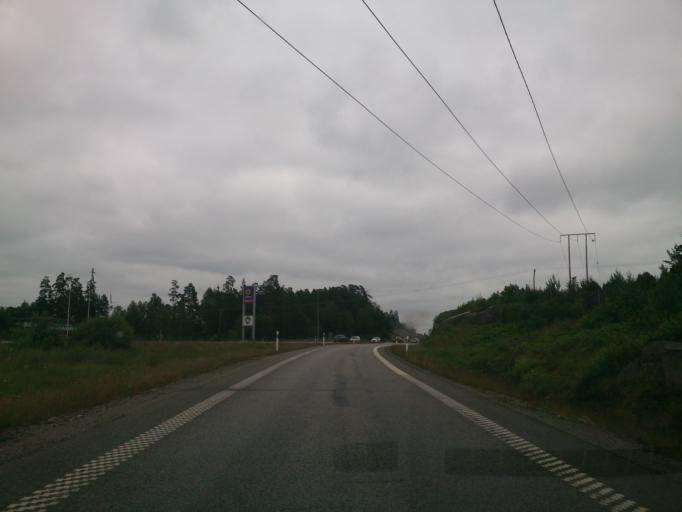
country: SE
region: OEstergoetland
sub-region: Norrkopings Kommun
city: Kimstad
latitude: 58.4892
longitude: 15.9512
